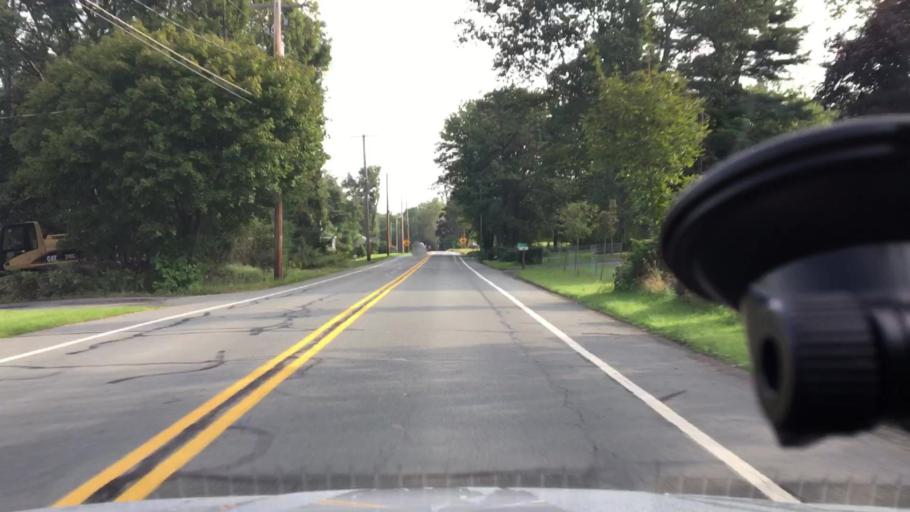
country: US
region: Pennsylvania
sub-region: Monroe County
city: Mount Pocono
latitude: 41.1211
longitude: -75.3143
